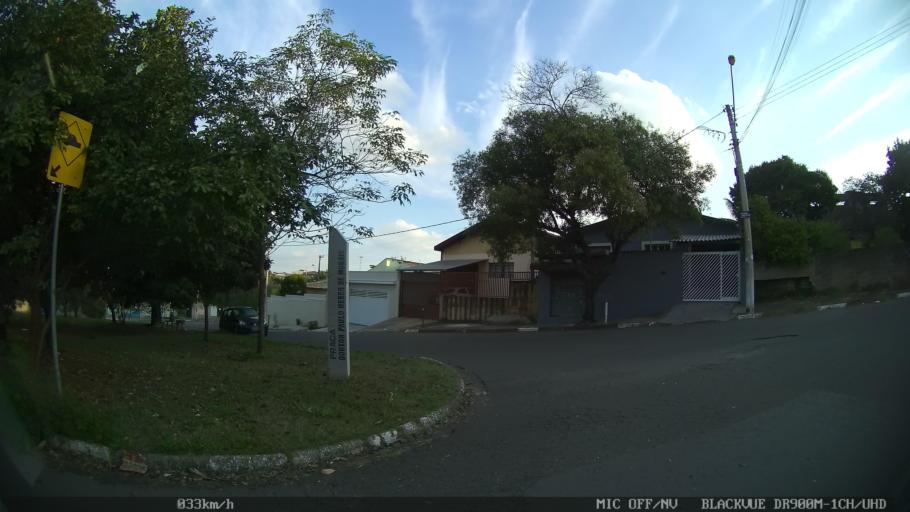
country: BR
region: Sao Paulo
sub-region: Hortolandia
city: Hortolandia
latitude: -22.8954
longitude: -47.1571
